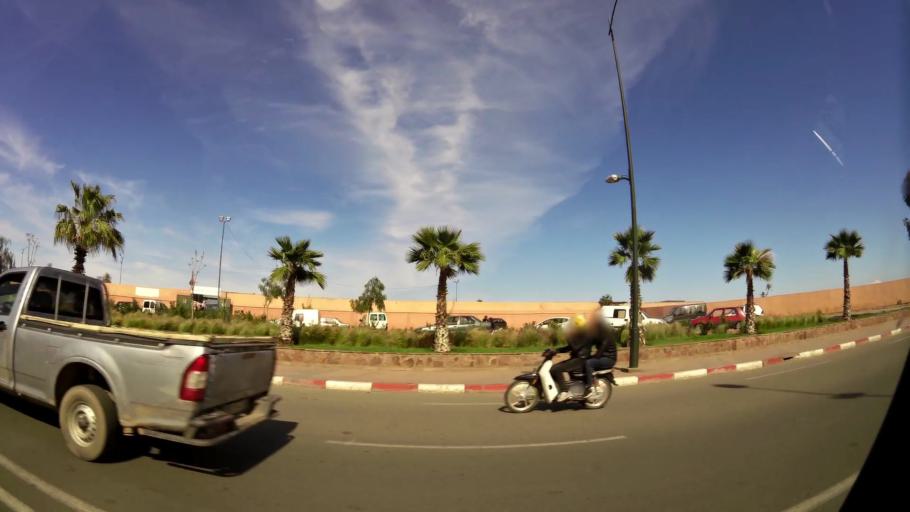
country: MA
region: Marrakech-Tensift-Al Haouz
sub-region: Marrakech
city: Marrakesh
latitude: 31.6260
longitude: -7.9708
